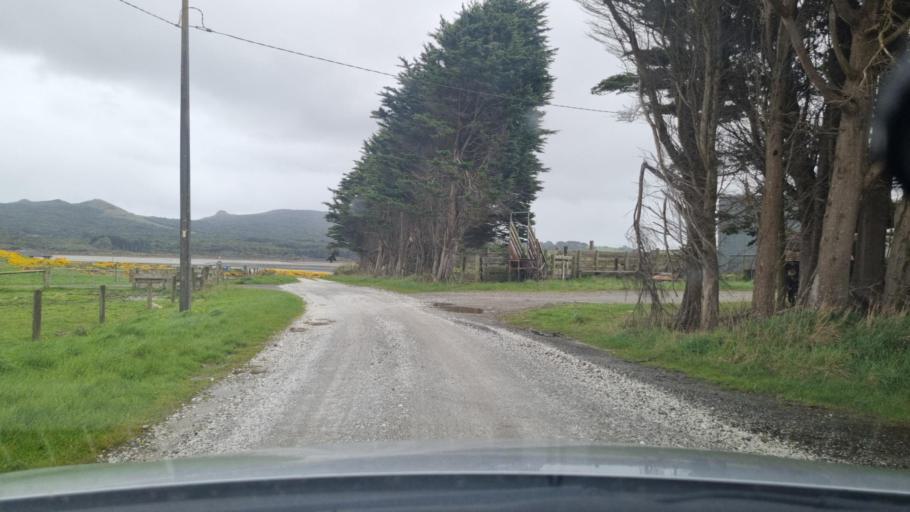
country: NZ
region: Southland
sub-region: Invercargill City
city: Bluff
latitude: -46.5379
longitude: 168.2894
